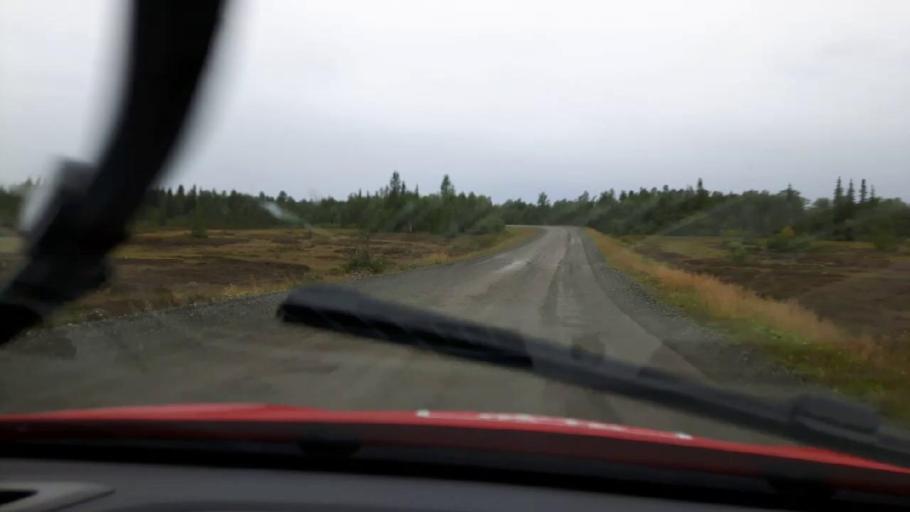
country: NO
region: Nord-Trondelag
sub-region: Meraker
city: Meraker
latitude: 63.5842
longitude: 12.2679
